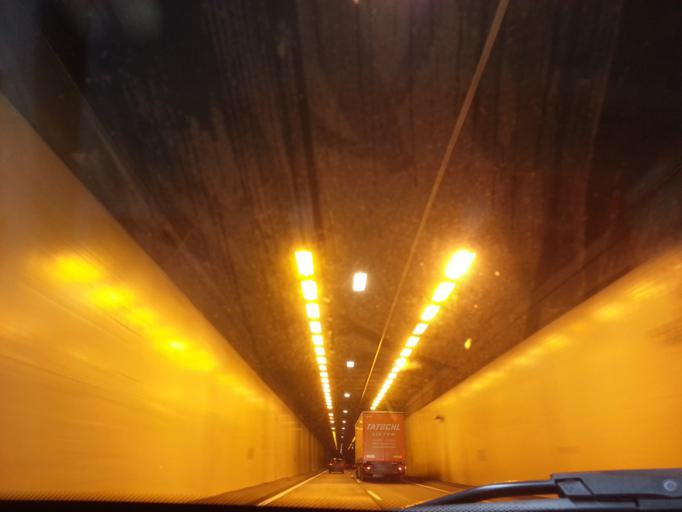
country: AT
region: Styria
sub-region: Politischer Bezirk Leoben
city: Wald am Schoberpass
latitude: 47.4530
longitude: 14.6688
